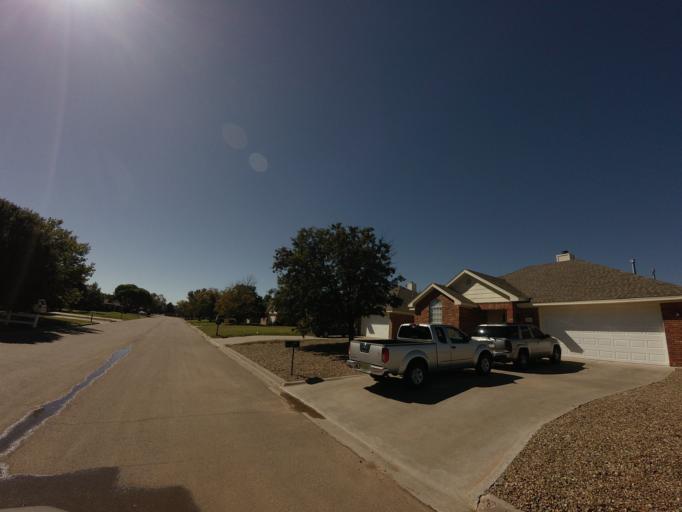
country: US
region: New Mexico
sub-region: Curry County
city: Clovis
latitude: 34.4260
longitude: -103.1893
